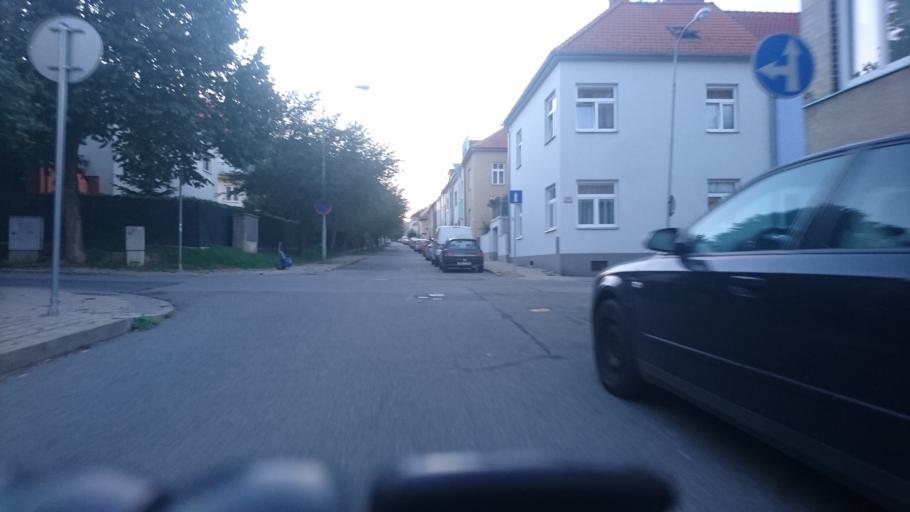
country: CZ
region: South Moravian
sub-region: Mesto Brno
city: Mokra Hora
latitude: 49.2428
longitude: 16.5807
